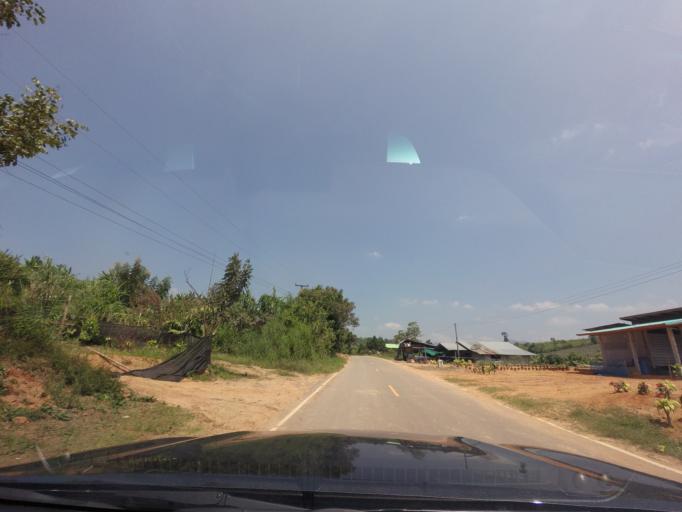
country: TH
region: Loei
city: Na Haeo
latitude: 17.5437
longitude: 100.8786
